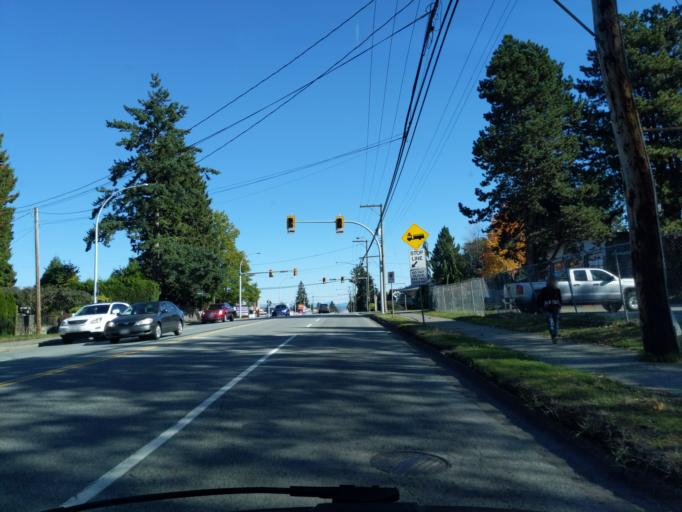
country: CA
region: British Columbia
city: Port Moody
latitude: 49.1987
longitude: -122.8187
